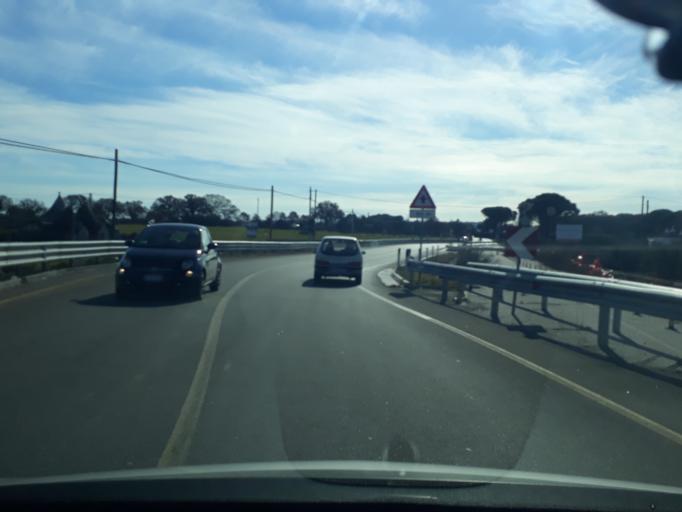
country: IT
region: Apulia
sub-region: Provincia di Bari
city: Locorotondo
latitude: 40.7367
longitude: 17.3325
